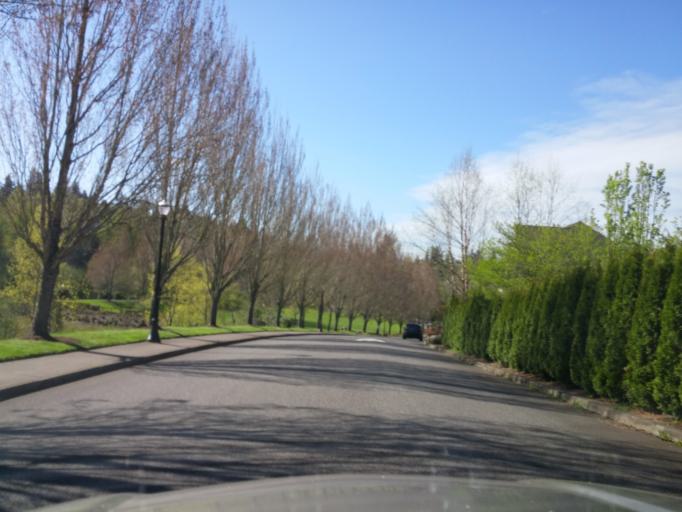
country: US
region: Oregon
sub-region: Washington County
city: West Haven
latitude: 45.5378
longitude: -122.7836
